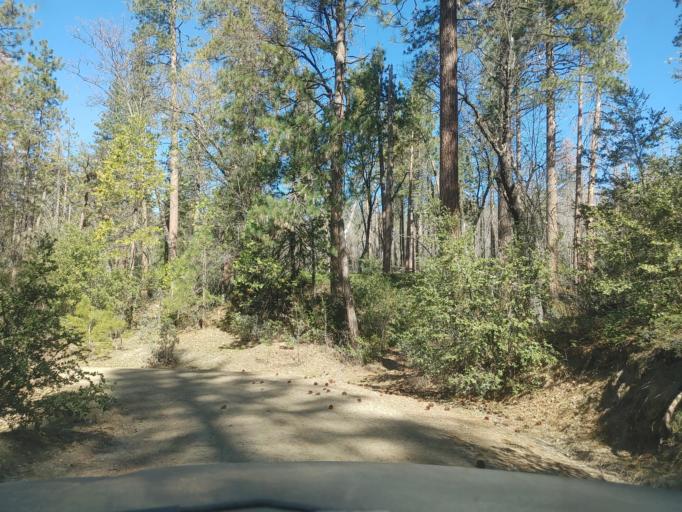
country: US
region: California
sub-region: Madera County
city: Ahwahnee
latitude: 37.4229
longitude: -119.6749
